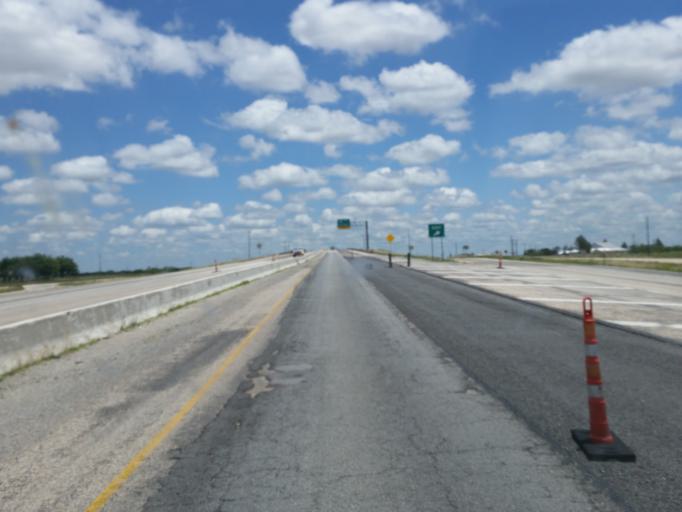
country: US
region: Texas
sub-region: Nolan County
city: Roscoe
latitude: 32.4522
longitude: -100.5254
